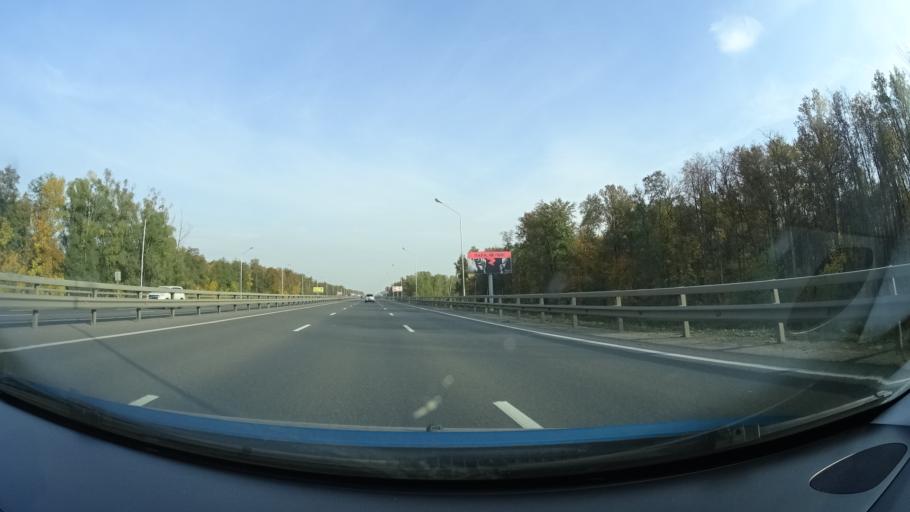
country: RU
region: Bashkortostan
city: Avdon
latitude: 54.6701
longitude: 55.8396
